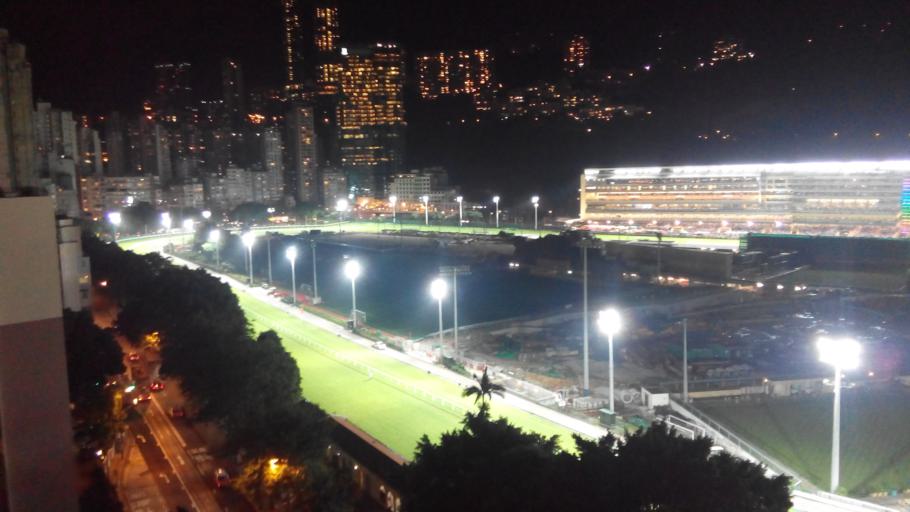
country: HK
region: Wanchai
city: Wan Chai
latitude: 22.2744
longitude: 114.1822
